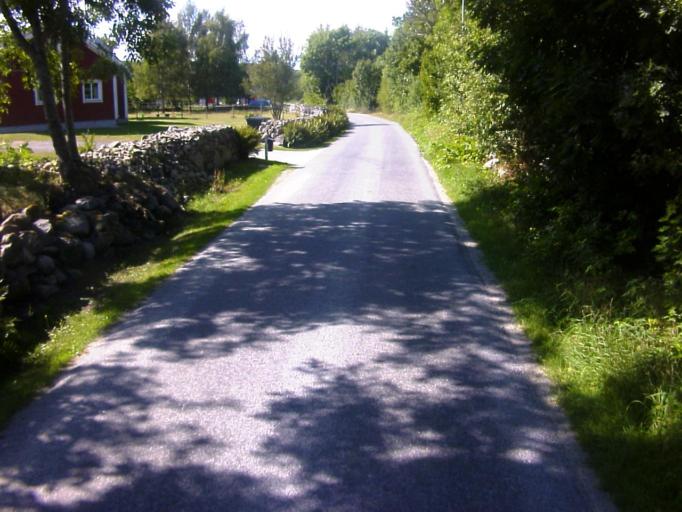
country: SE
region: Blekinge
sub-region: Solvesborgs Kommun
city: Soelvesborg
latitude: 56.1058
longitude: 14.6146
